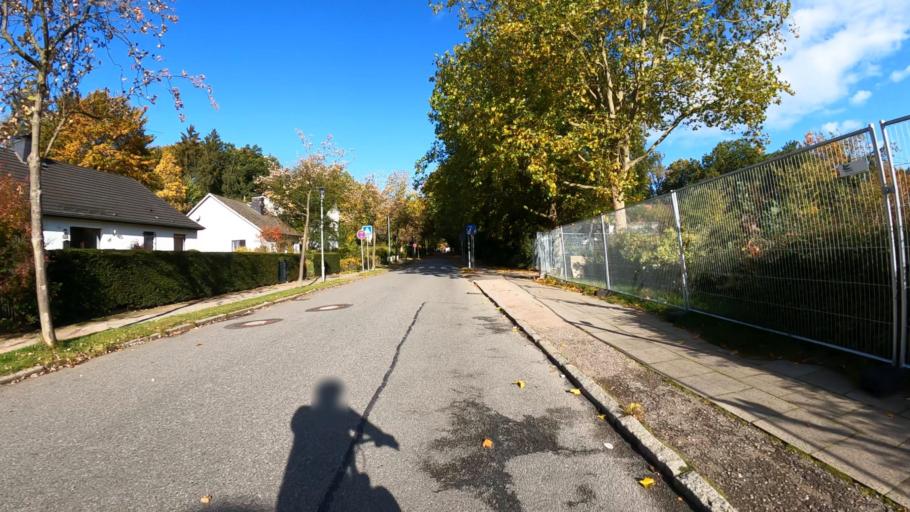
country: DE
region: Schleswig-Holstein
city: Ahrensburg
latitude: 53.6622
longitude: 10.2436
